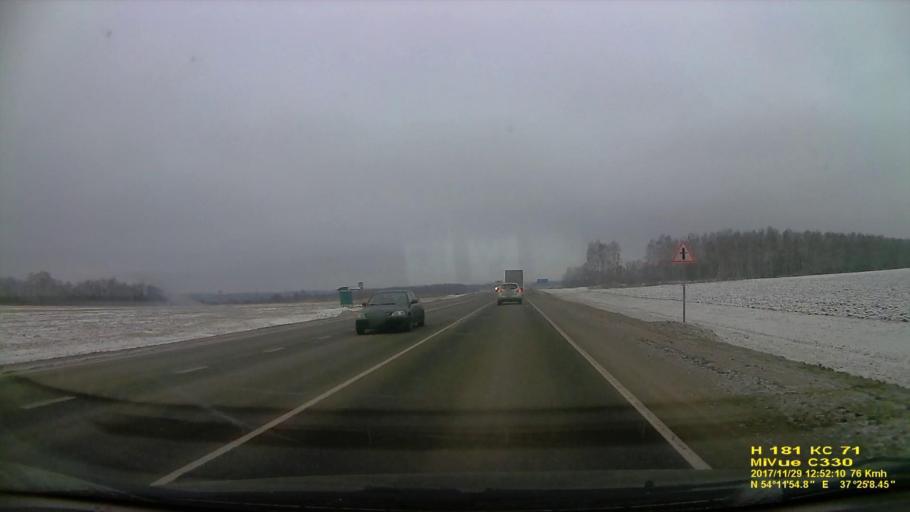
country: RU
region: Tula
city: Barsuki
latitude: 54.1987
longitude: 37.4188
